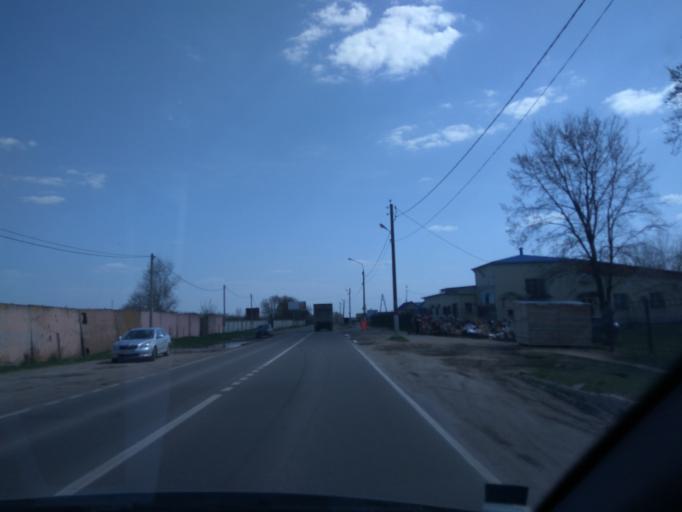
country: RU
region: Moskovskaya
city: Ramenskoye
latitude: 55.5515
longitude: 38.2583
